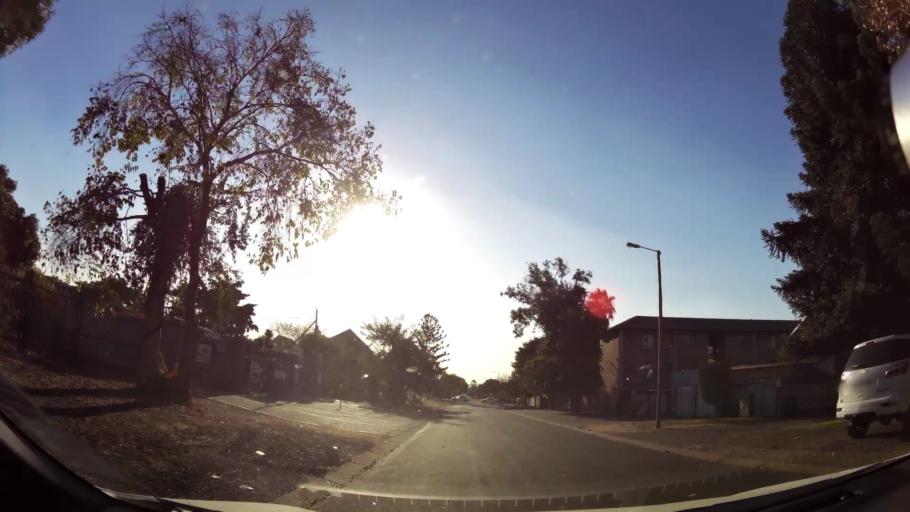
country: ZA
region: North-West
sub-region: Bojanala Platinum District Municipality
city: Rustenburg
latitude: -25.6795
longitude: 27.2357
